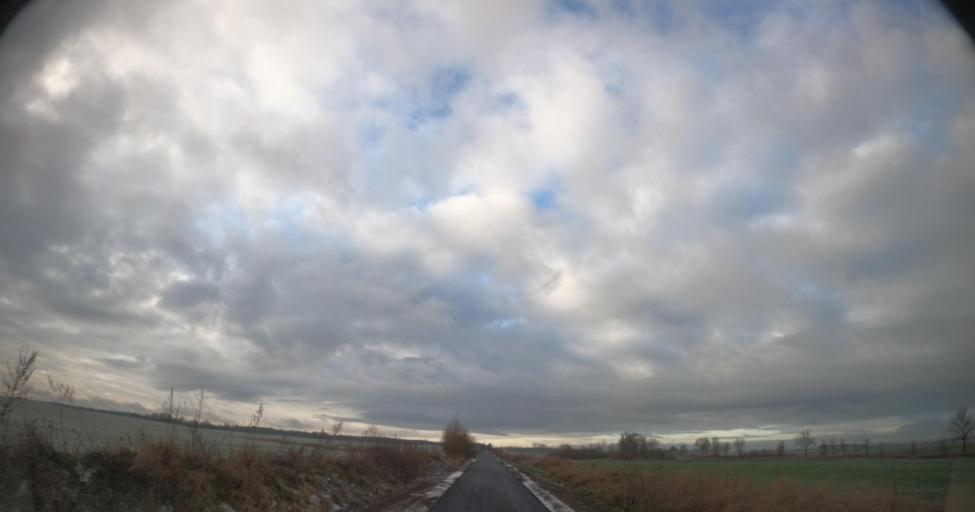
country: PL
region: West Pomeranian Voivodeship
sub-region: Powiat mysliborski
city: Barlinek
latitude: 52.9853
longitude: 15.1135
